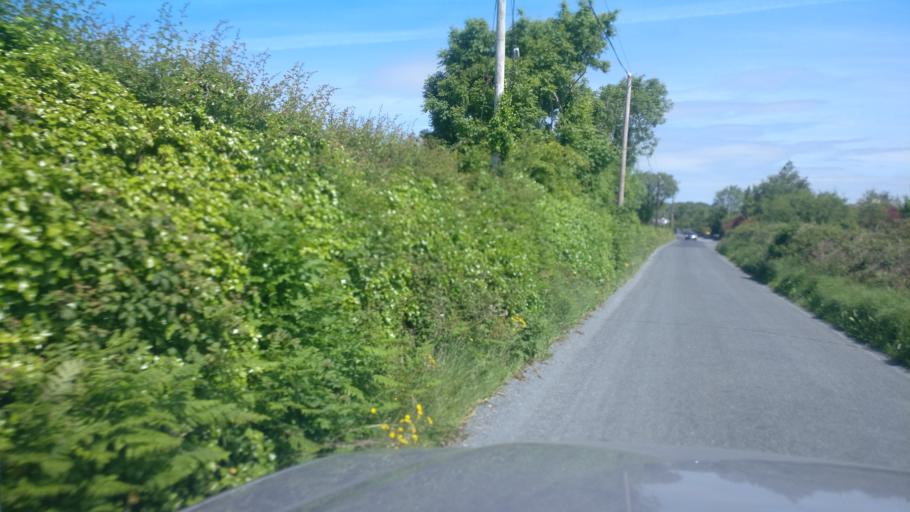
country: IE
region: Connaught
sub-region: County Galway
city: Gort
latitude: 53.0817
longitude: -8.8023
